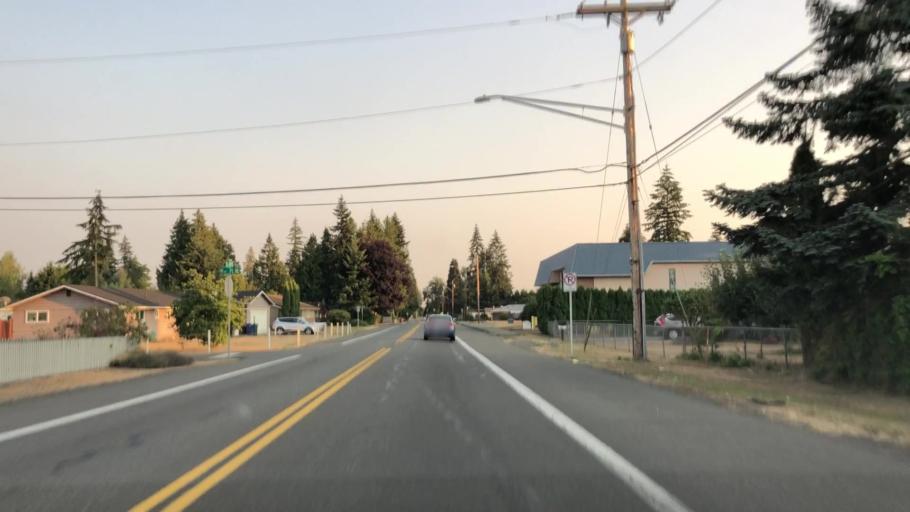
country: US
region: Washington
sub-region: Snohomish County
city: Marysville
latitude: 48.0789
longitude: -122.1622
